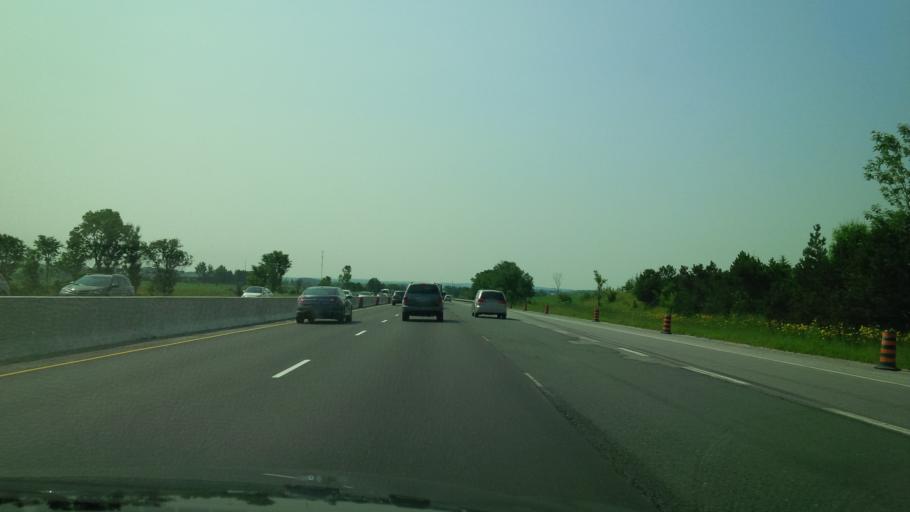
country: CA
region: Ontario
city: Bradford West Gwillimbury
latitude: 44.0961
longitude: -79.6301
